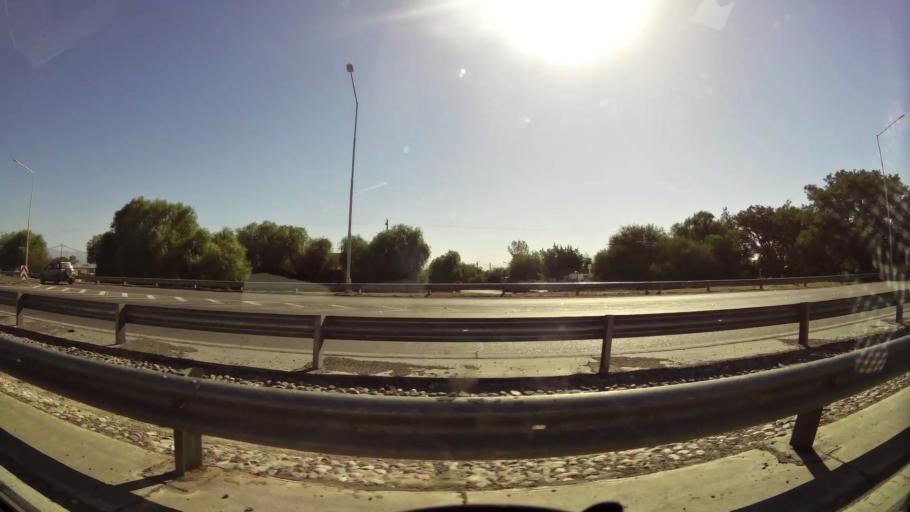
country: AR
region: San Juan
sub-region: Departamento de Santa Lucia
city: Santa Lucia
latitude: -31.5302
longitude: -68.5039
